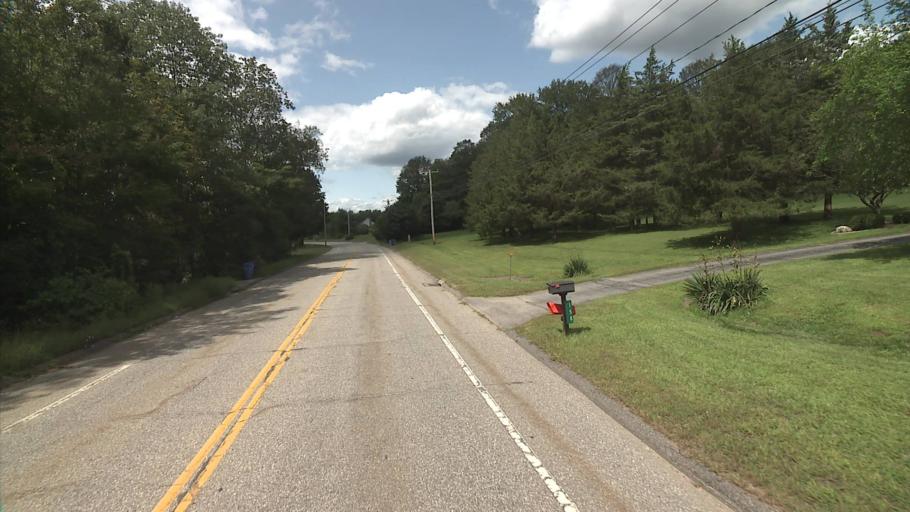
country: US
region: Connecticut
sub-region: New London County
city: Baltic
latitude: 41.6271
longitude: -72.1203
